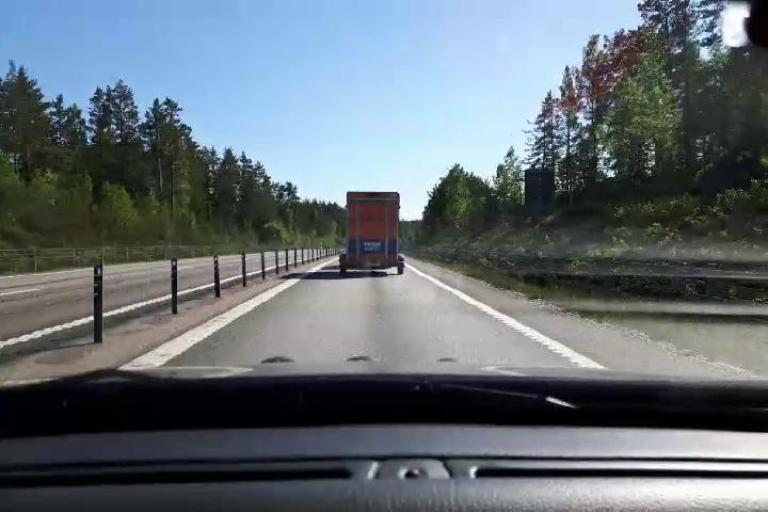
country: SE
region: Gaevleborg
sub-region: Soderhamns Kommun
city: Ljusne
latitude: 61.1451
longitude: 17.0321
